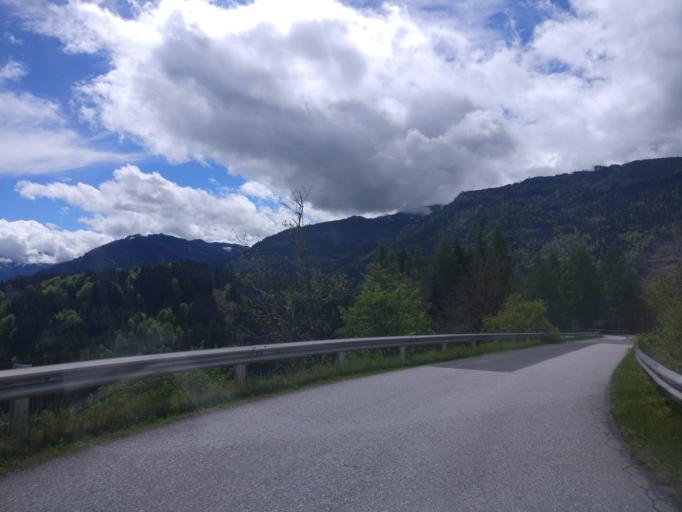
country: AT
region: Salzburg
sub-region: Politischer Bezirk Sankt Johann im Pongau
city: Bischofshofen
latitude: 47.4368
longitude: 13.2340
